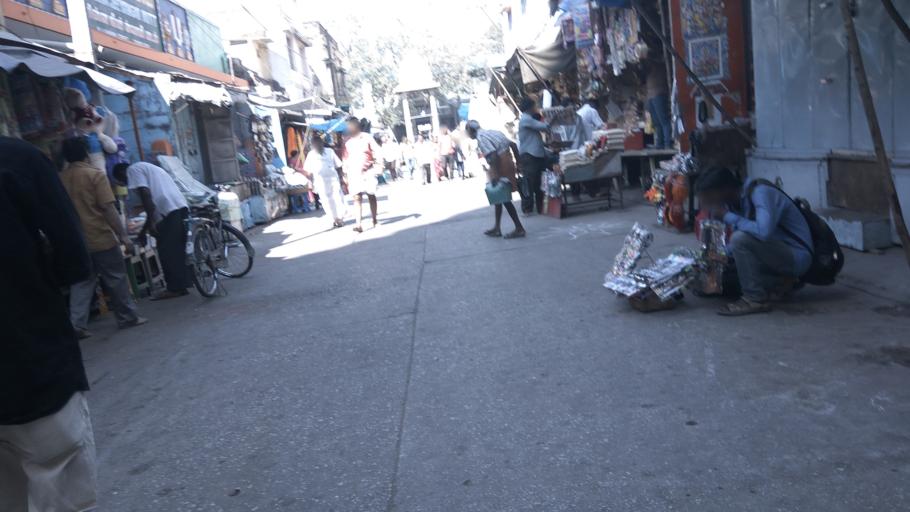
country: IN
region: Andhra Pradesh
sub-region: Chittoor
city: Tirupati
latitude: 13.6298
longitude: 79.4185
